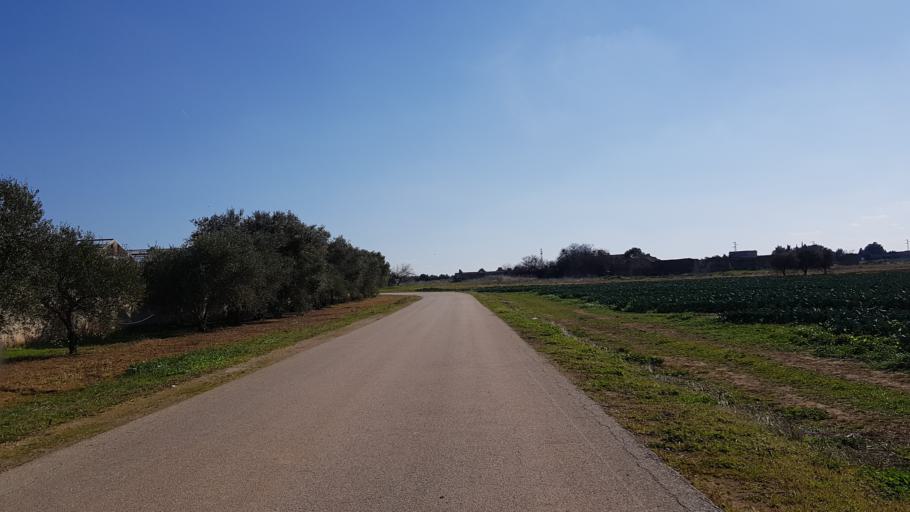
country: IT
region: Apulia
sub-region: Provincia di Brindisi
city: Mesagne
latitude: 40.6184
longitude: 17.8171
